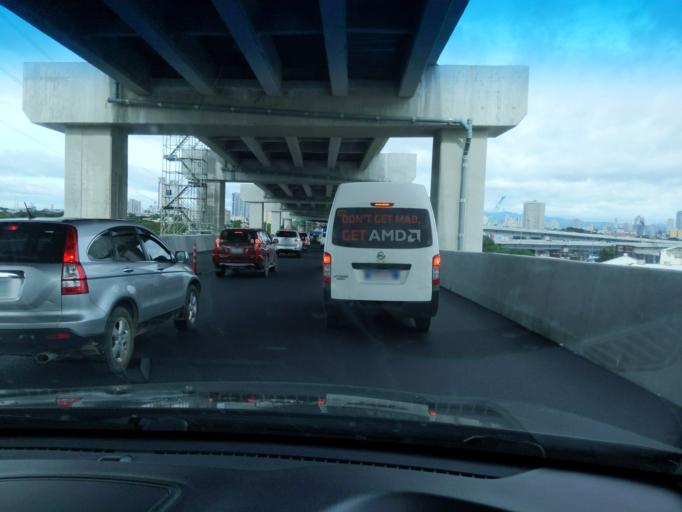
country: PH
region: Metro Manila
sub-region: City of Manila
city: Quiapo
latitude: 14.5883
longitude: 121.0074
